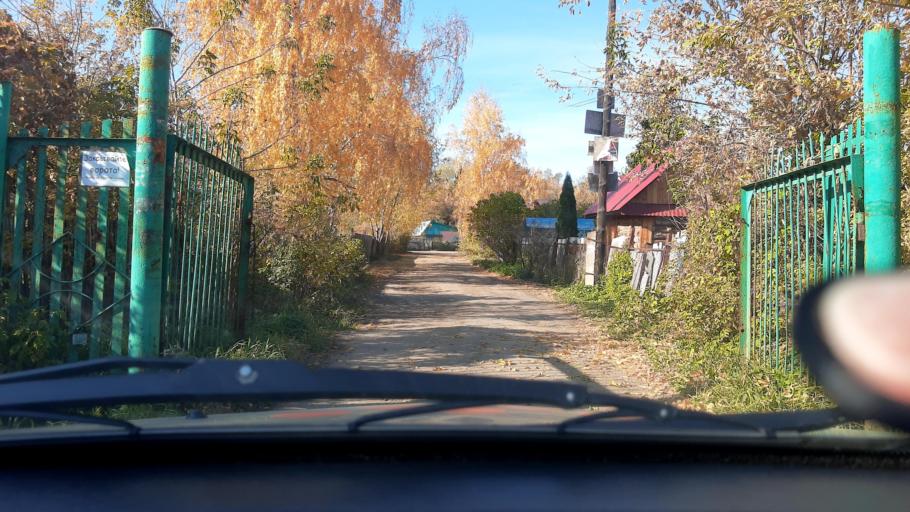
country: RU
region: Bashkortostan
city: Ufa
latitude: 54.8028
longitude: 56.1539
